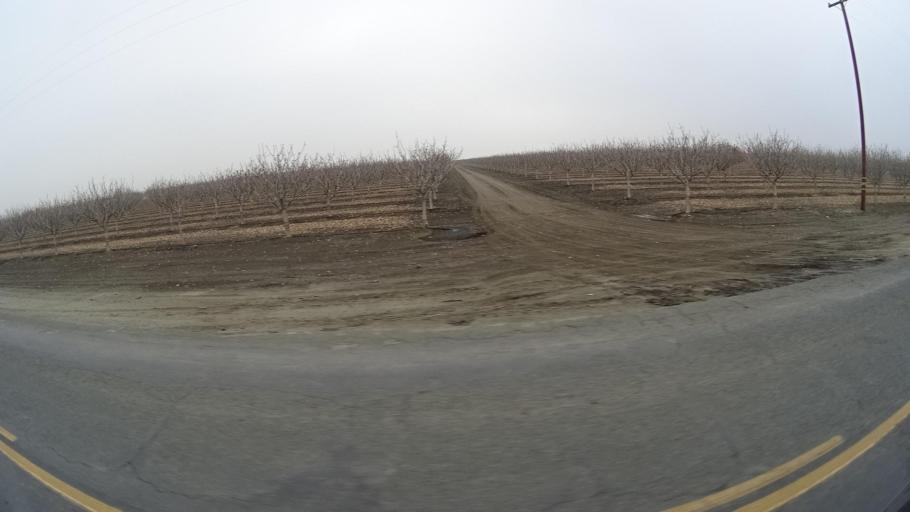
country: US
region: California
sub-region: Kern County
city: Buttonwillow
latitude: 35.3669
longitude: -119.4742
